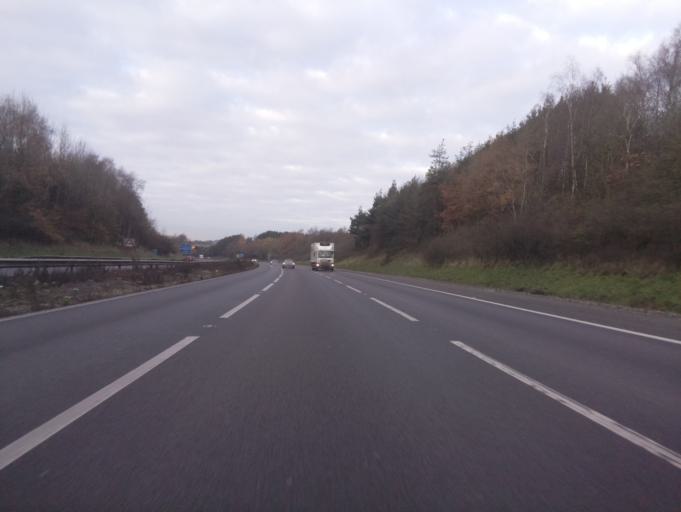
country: GB
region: England
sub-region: Worcestershire
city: Barnt Green
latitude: 52.3577
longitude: -2.0254
